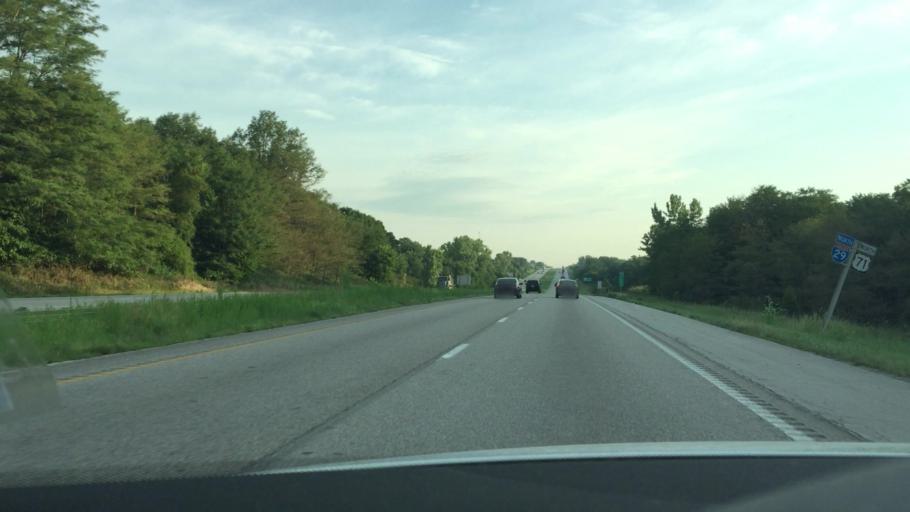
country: US
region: Missouri
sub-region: Platte County
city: Platte City
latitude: 39.3905
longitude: -94.7894
